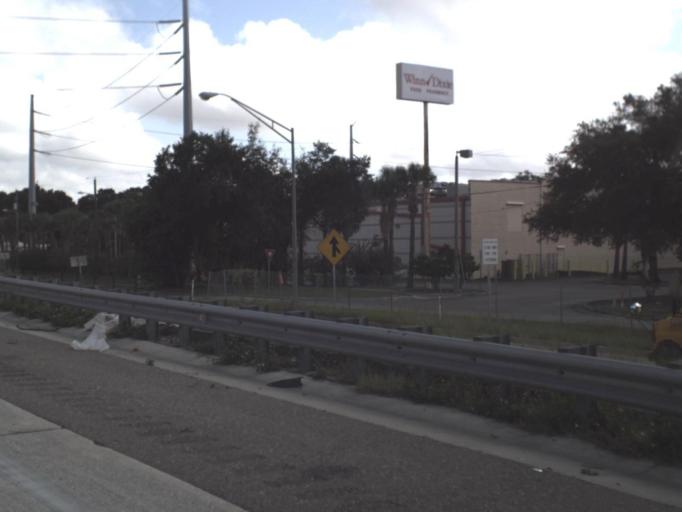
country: US
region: Florida
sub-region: Hillsborough County
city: Tampa
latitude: 27.9799
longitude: -82.4535
